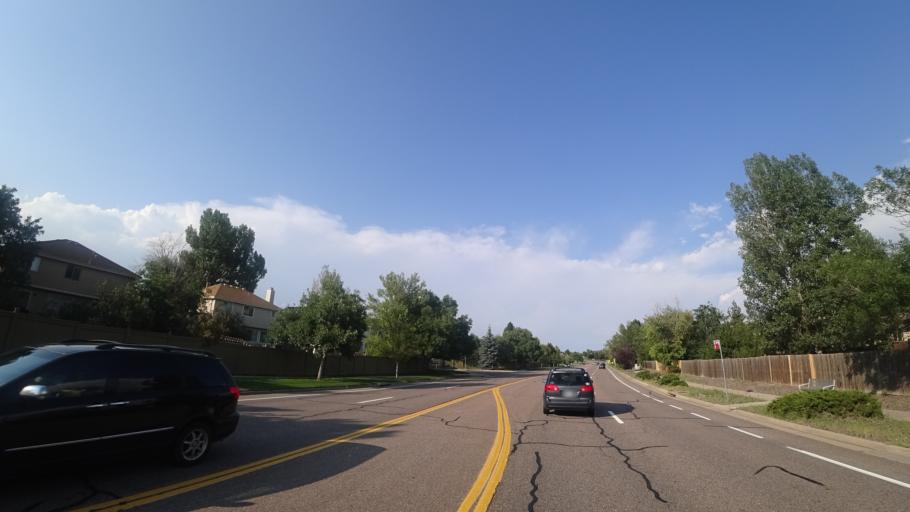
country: US
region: Colorado
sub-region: Arapahoe County
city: Dove Valley
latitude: 39.6152
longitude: -104.7436
